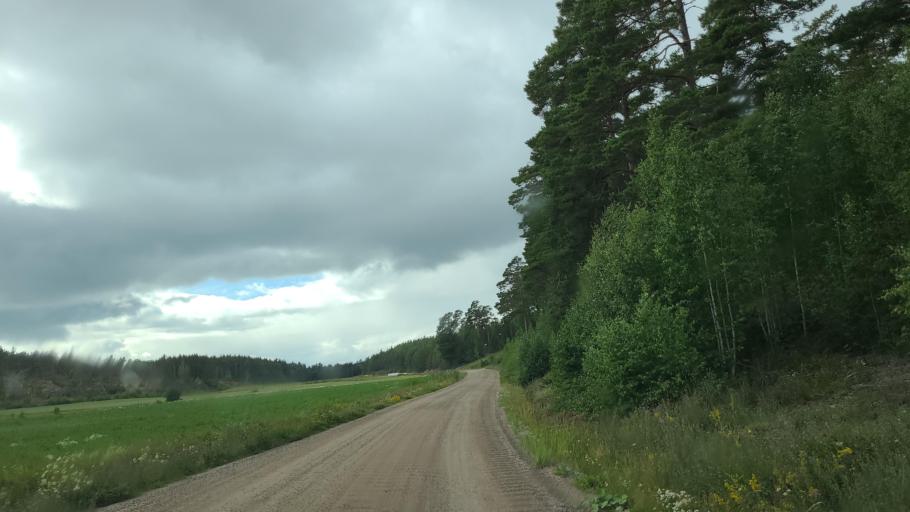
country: FI
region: Varsinais-Suomi
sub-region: Aboland-Turunmaa
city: Nagu
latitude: 60.2043
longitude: 21.8639
